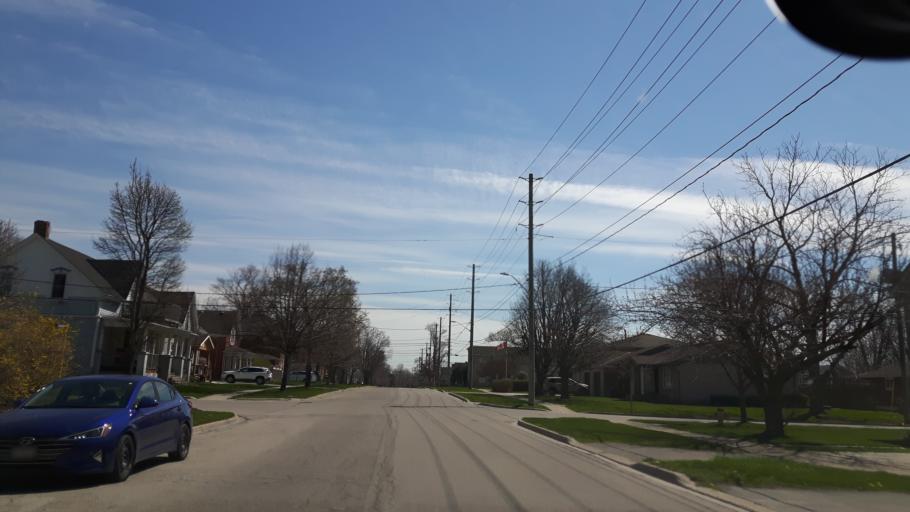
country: CA
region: Ontario
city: Goderich
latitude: 43.7444
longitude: -81.7046
